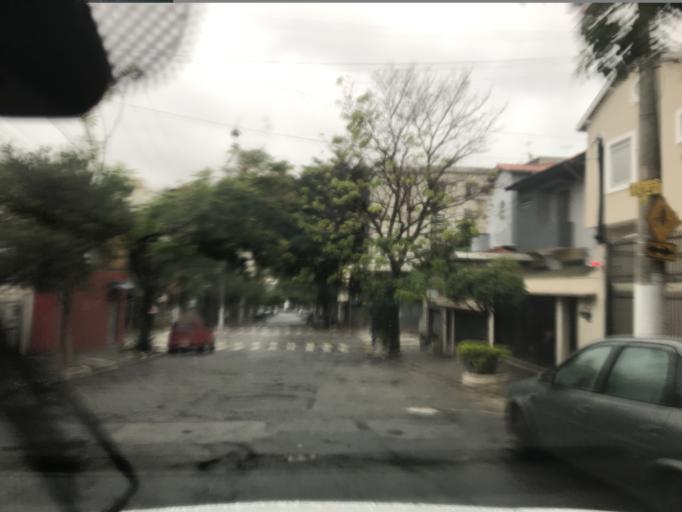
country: BR
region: Sao Paulo
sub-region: Sao Paulo
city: Sao Paulo
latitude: -23.5301
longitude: -46.6835
